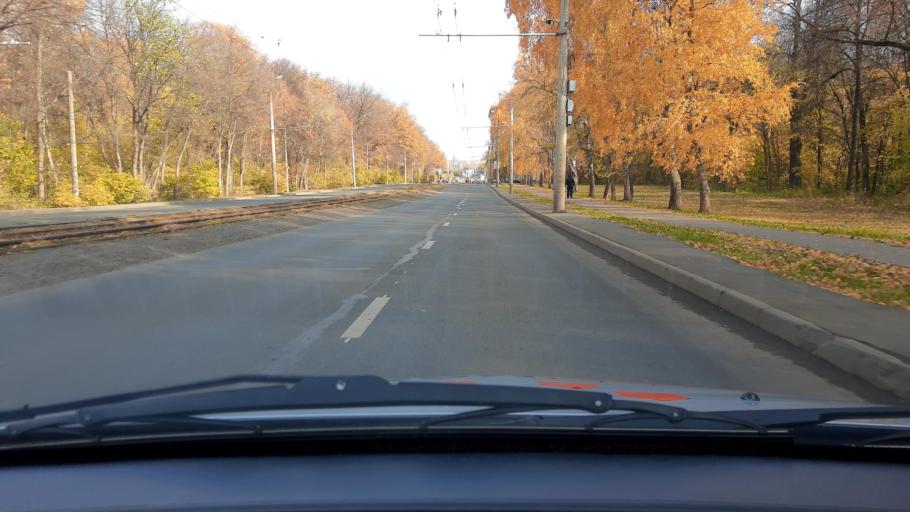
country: RU
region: Bashkortostan
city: Ufa
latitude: 54.7964
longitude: 56.0491
